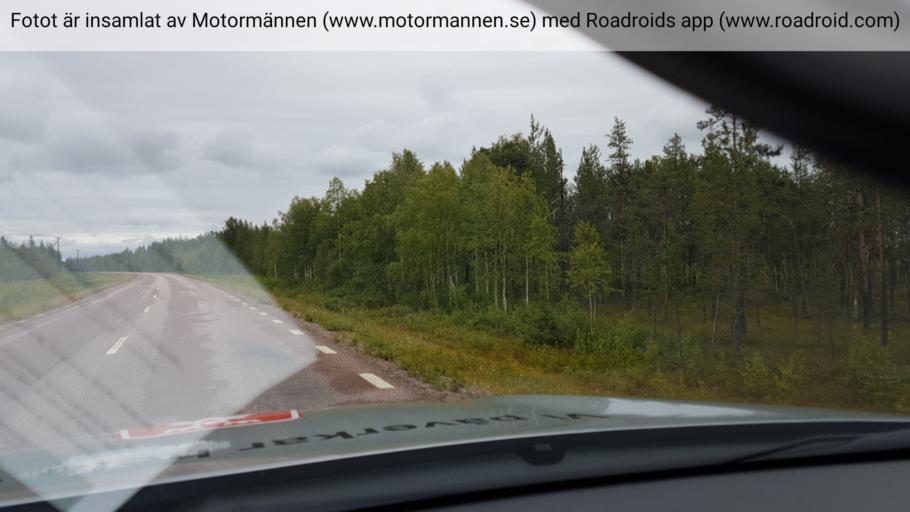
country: SE
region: Norrbotten
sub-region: Pajala Kommun
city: Pajala
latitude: 67.1068
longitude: 22.5975
